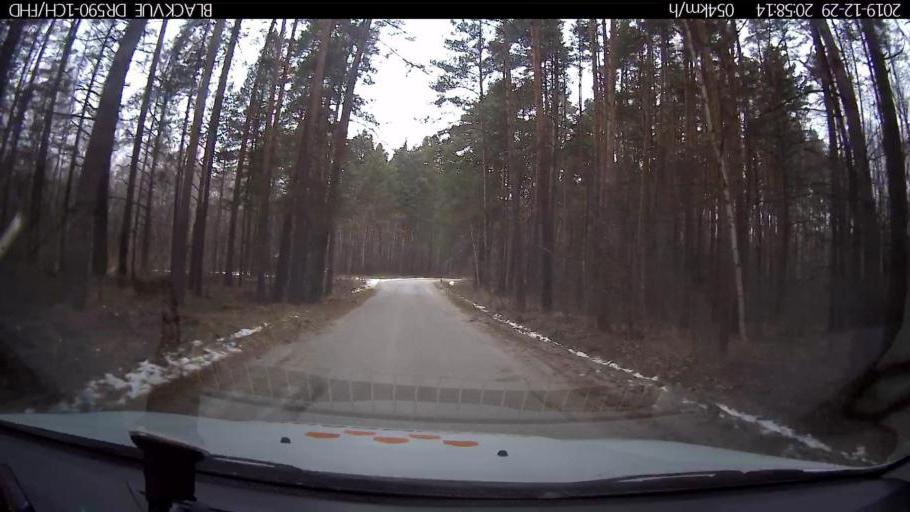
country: RU
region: Nizjnij Novgorod
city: Afonino
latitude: 56.1672
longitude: 43.9875
